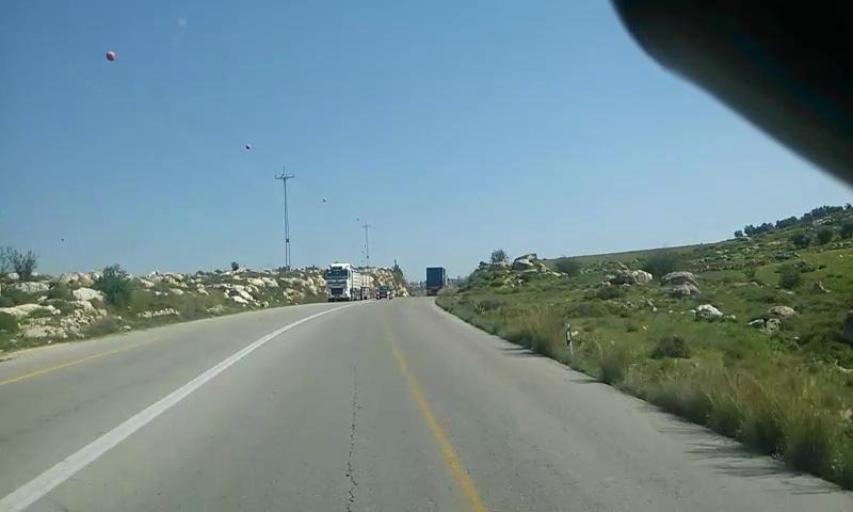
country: PS
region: West Bank
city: Tarqumya
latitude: 31.5612
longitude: 35.0032
